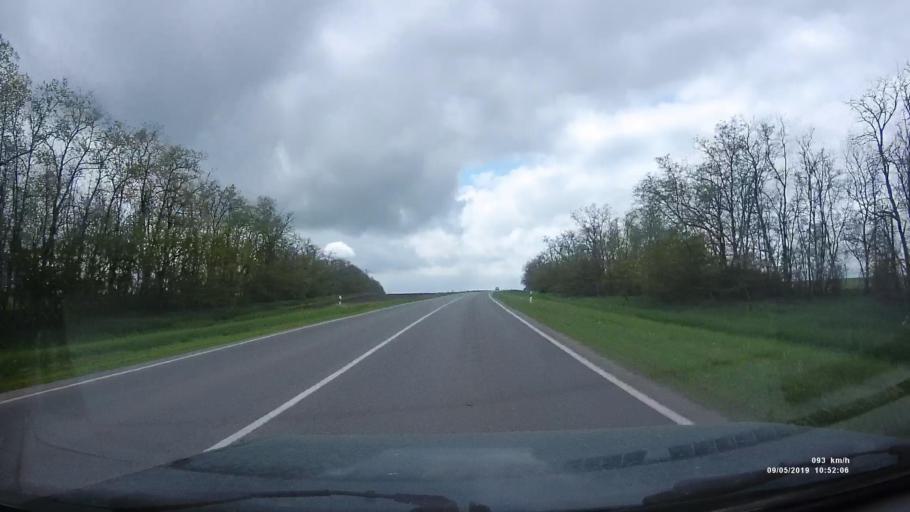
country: RU
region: Rostov
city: Peshkovo
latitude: 46.9053
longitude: 39.3548
